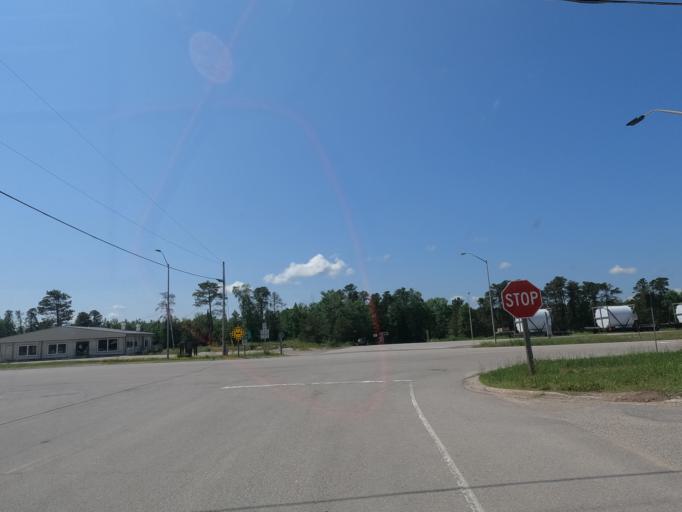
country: CA
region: Ontario
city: Dryden
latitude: 49.8537
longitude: -93.3642
